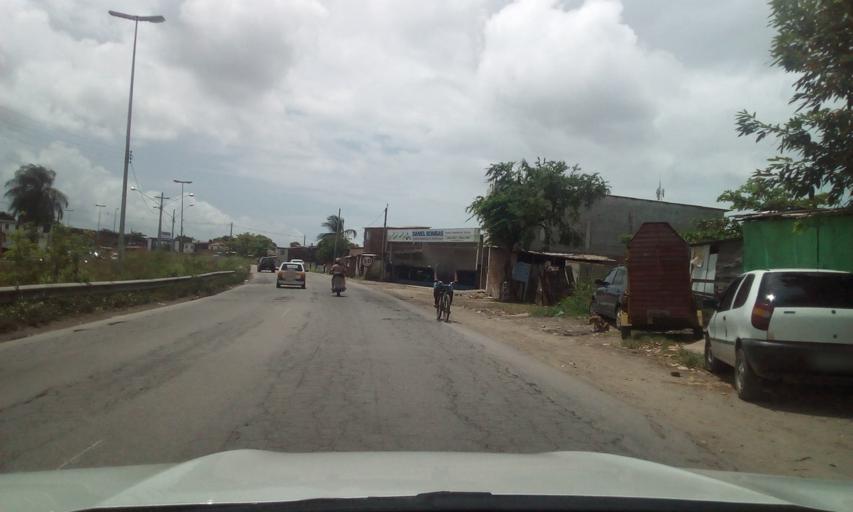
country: BR
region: Pernambuco
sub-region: Recife
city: Recife
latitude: -8.0837
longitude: -34.9439
